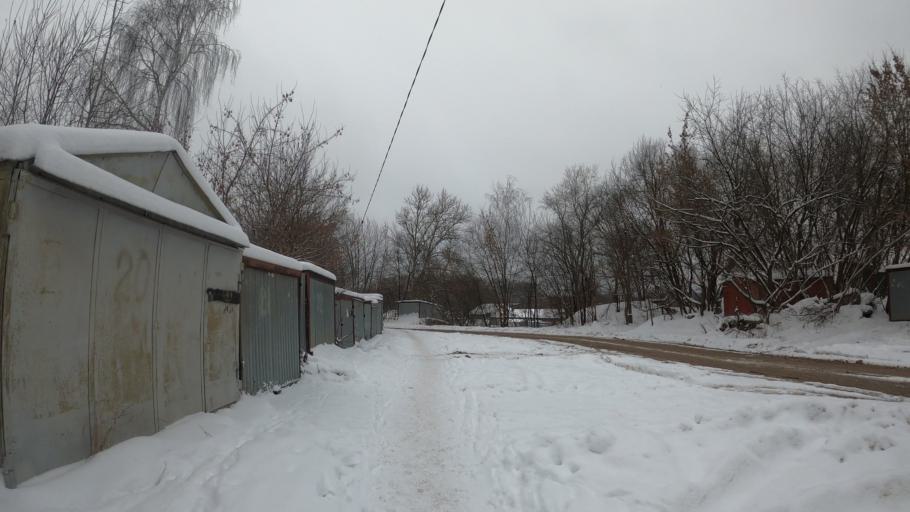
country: RU
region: Moskovskaya
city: Dolgoprudnyy
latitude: 55.9543
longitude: 37.4874
